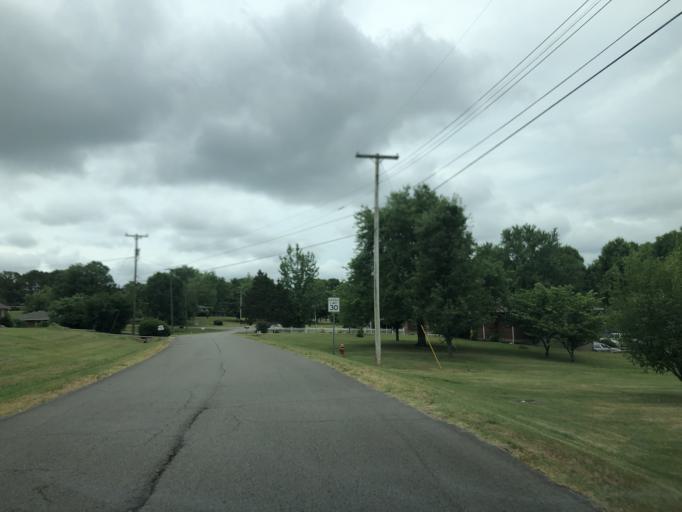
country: US
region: Tennessee
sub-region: Davidson County
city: Goodlettsville
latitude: 36.2685
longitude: -86.7633
